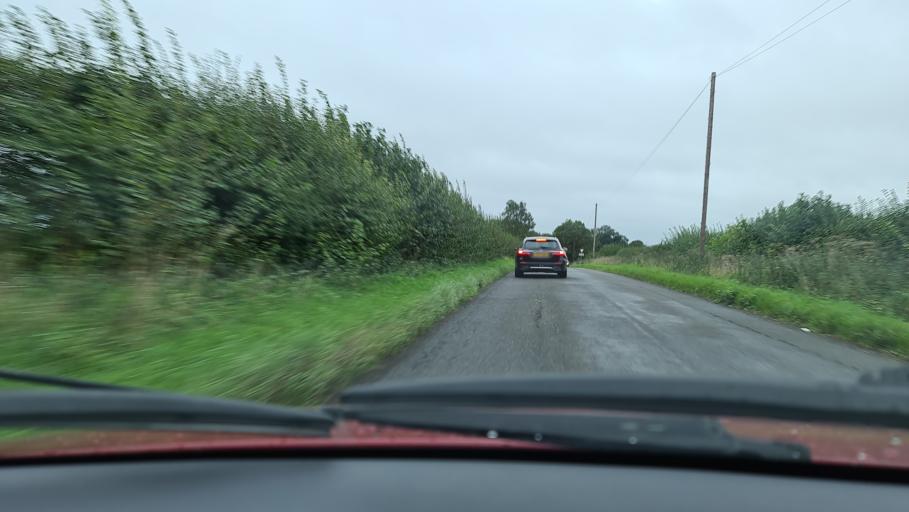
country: GB
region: England
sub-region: Oxfordshire
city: Bicester
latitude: 51.9288
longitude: -1.1896
